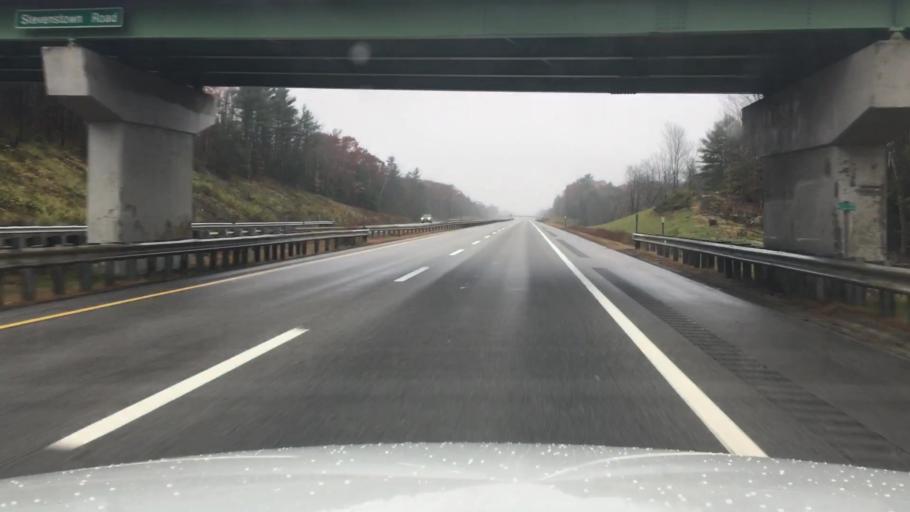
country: US
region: Maine
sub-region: Sagadahoc County
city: Richmond
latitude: 44.1551
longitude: -69.9015
